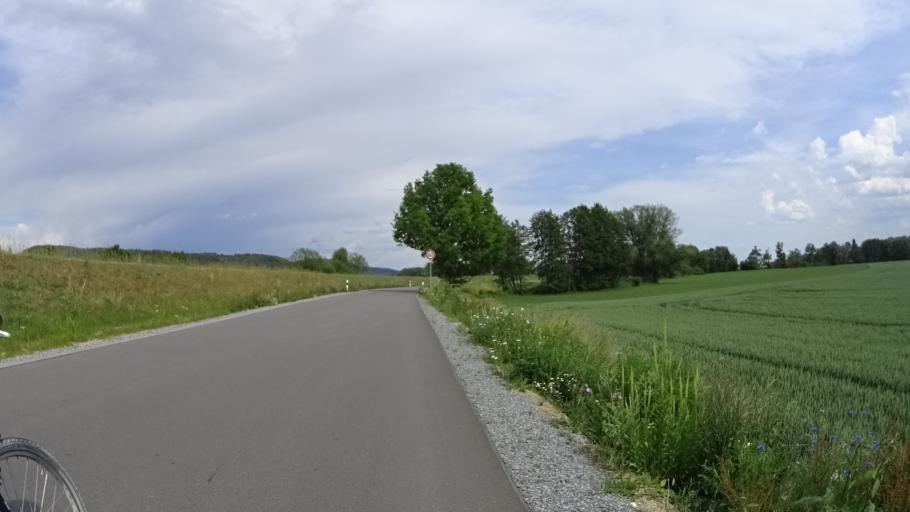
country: DE
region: Bavaria
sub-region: Upper Palatinate
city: Worth an der Donau
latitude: 48.9936
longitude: 12.3972
